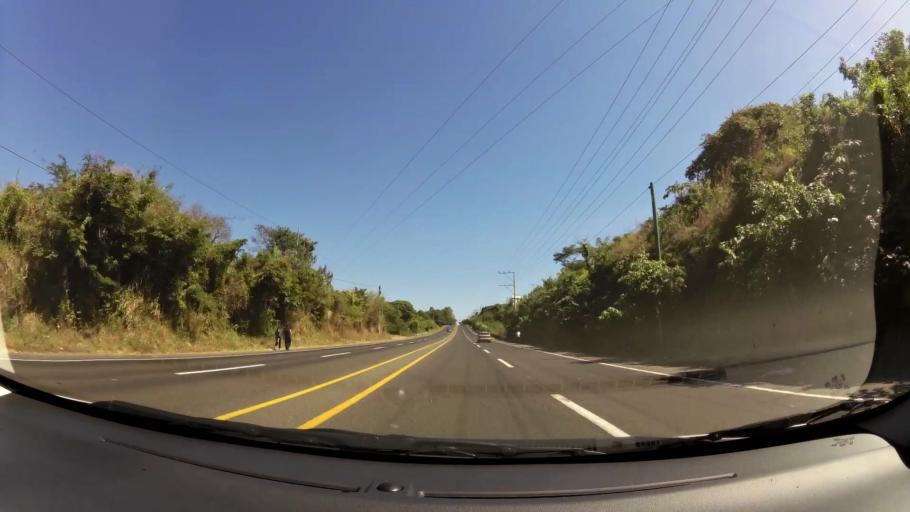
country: SV
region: Ahuachapan
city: Atiquizaya
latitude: 13.9710
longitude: -89.7490
